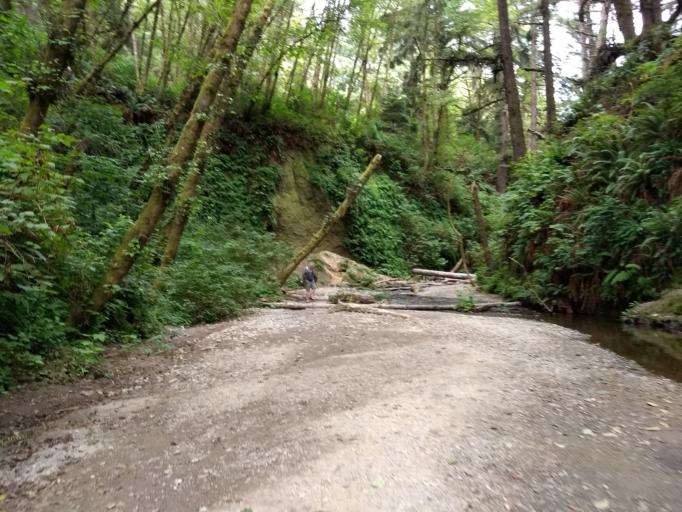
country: US
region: California
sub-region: Humboldt County
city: Westhaven-Moonstone
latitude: 41.4037
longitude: -124.0637
